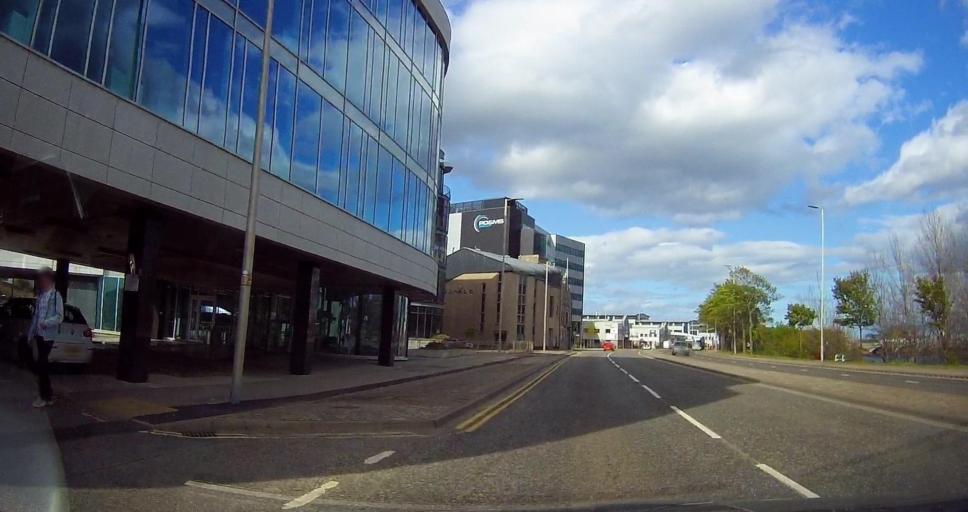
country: GB
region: Scotland
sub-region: Aberdeen City
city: Aberdeen
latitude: 57.1378
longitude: -2.0959
